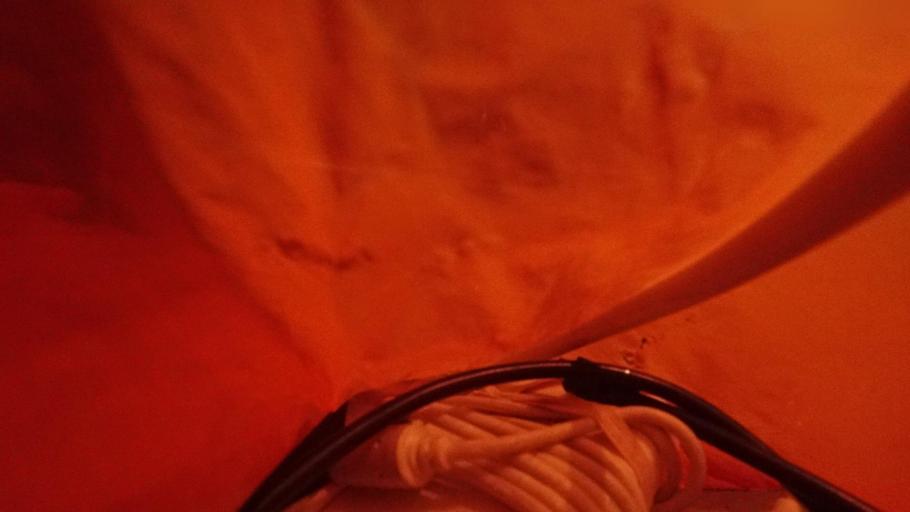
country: RU
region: Jewish Autonomous Oblast
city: Khingansk
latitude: 49.1650
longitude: 130.7936
